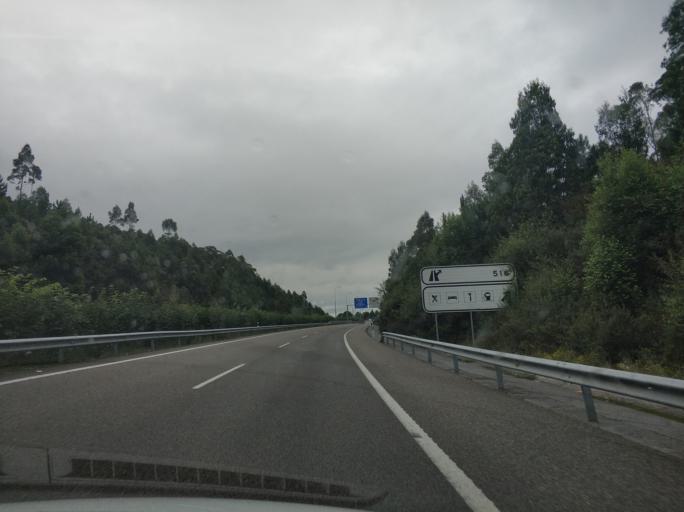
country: ES
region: Galicia
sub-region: Provincia de Lugo
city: Barreiros
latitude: 43.5351
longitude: -7.1450
